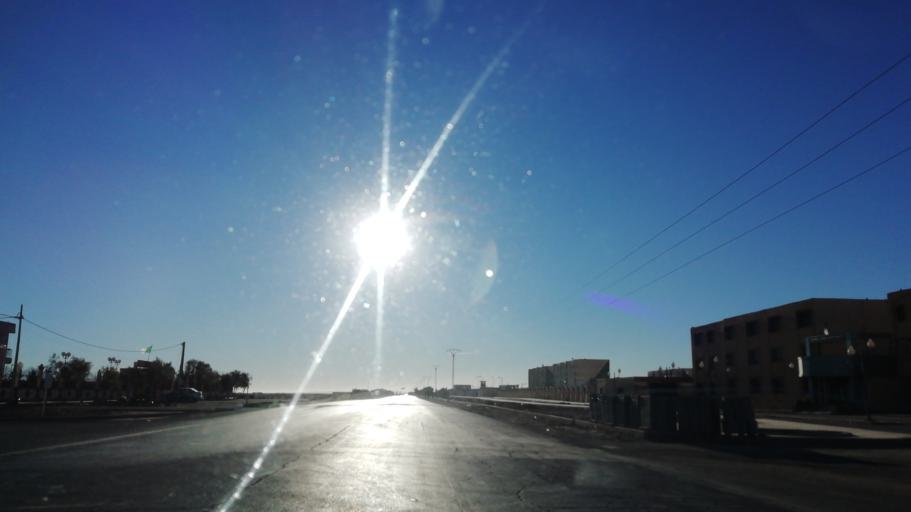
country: DZ
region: Saida
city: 'Ain el Hadjar
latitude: 34.0265
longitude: 0.0964
